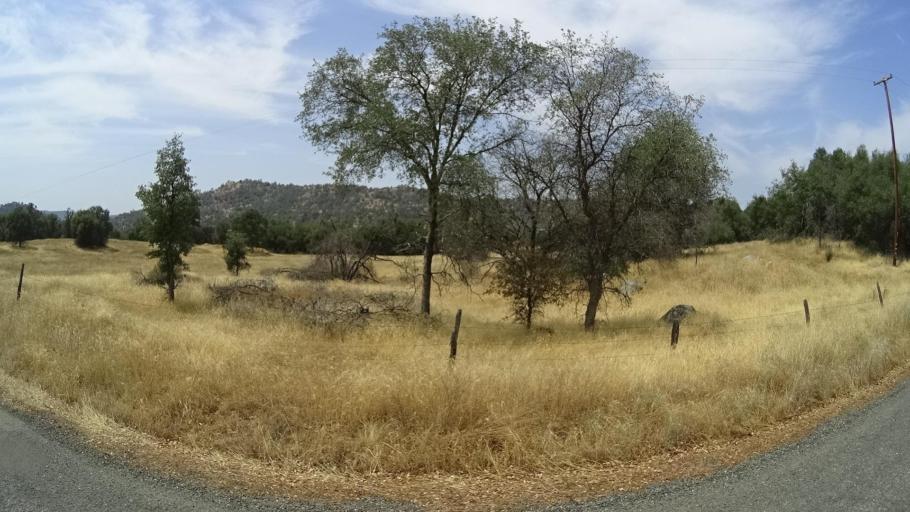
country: US
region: California
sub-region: Madera County
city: Ahwahnee
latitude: 37.3943
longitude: -119.8311
